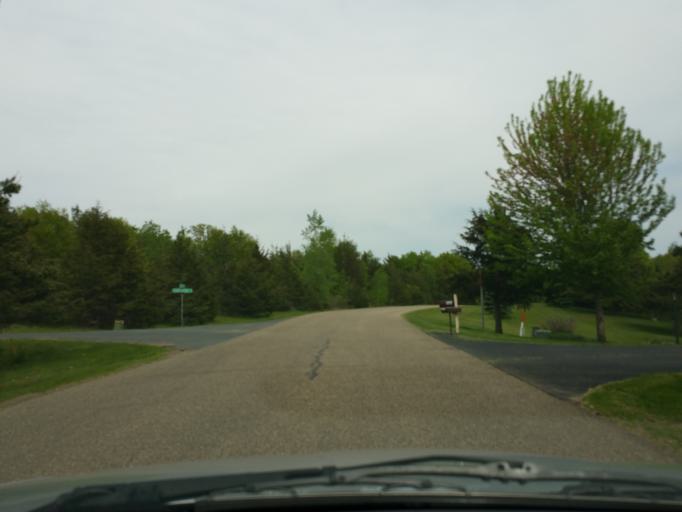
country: US
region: Wisconsin
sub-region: Saint Croix County
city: Hudson
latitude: 44.9488
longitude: -92.6843
